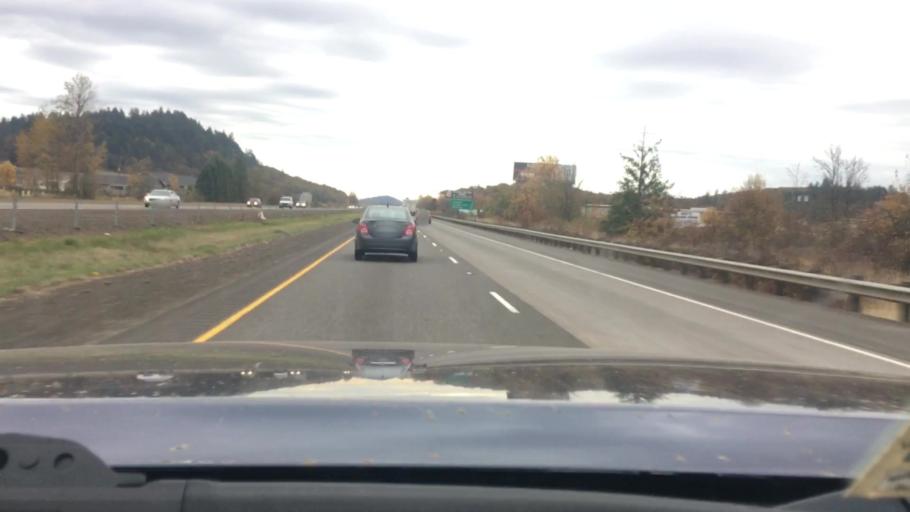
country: US
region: Oregon
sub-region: Lane County
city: Springfield
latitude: 43.9839
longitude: -123.0082
